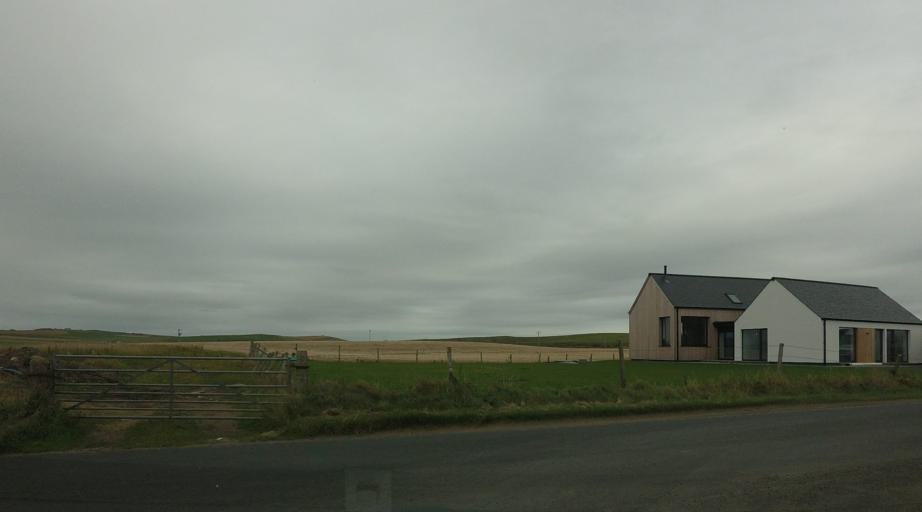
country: GB
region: Scotland
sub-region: Orkney Islands
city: Stromness
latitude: 59.0503
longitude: -3.3333
